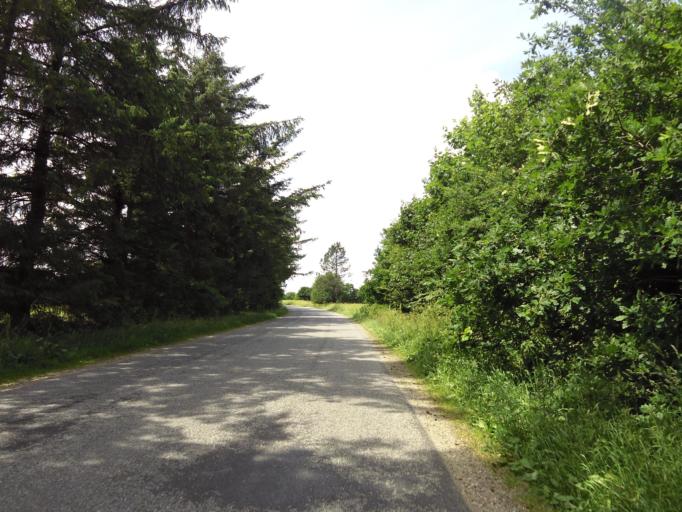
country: DK
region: South Denmark
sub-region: Esbjerg Kommune
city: Ribe
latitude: 55.2627
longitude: 8.8804
